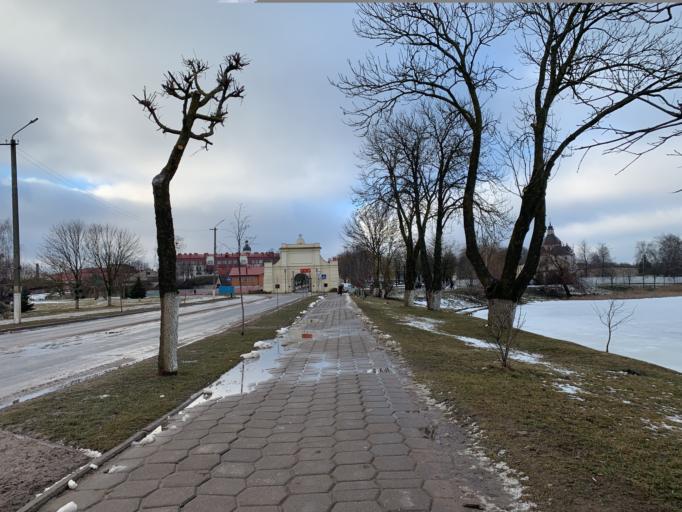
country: BY
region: Minsk
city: Nyasvizh
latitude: 53.2174
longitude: 26.6870
